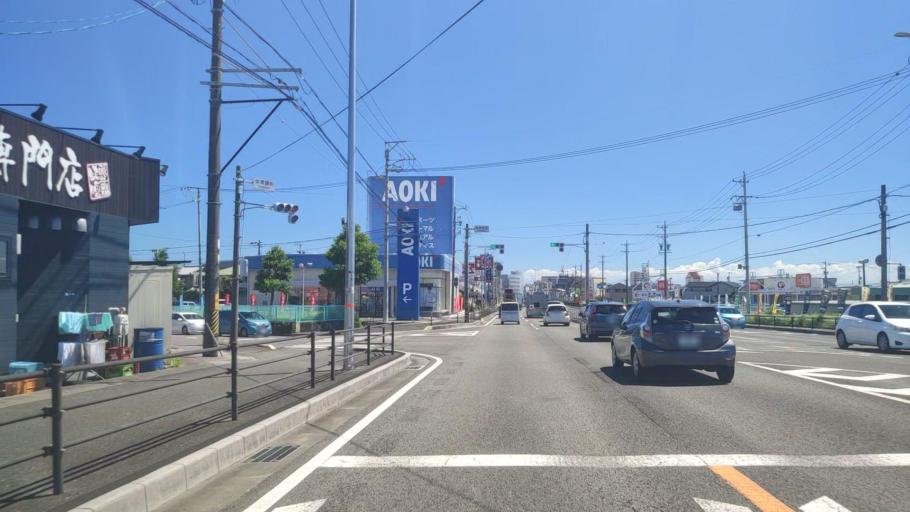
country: JP
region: Mie
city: Suzuka
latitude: 34.8425
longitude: 136.5888
